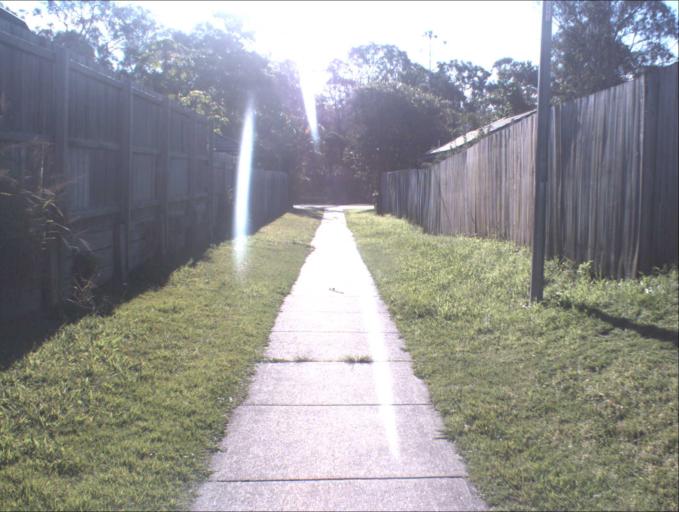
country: AU
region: Queensland
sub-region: Logan
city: Logan Reserve
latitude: -27.6948
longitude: 153.0902
